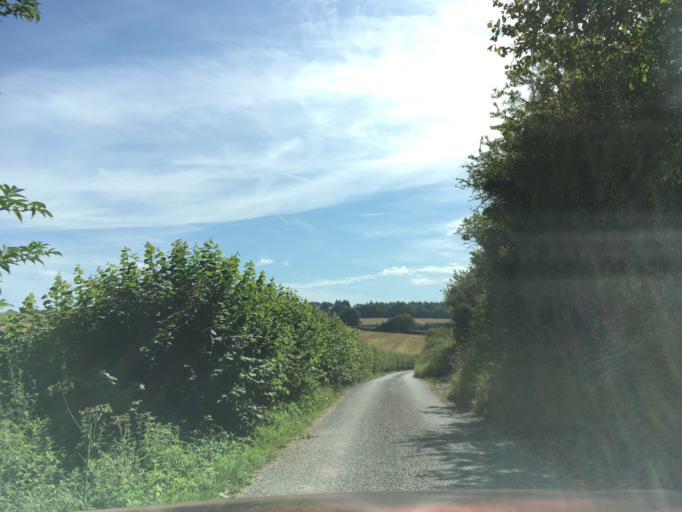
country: GB
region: England
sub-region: Hampshire
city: Highclere
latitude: 51.2893
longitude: -1.3628
